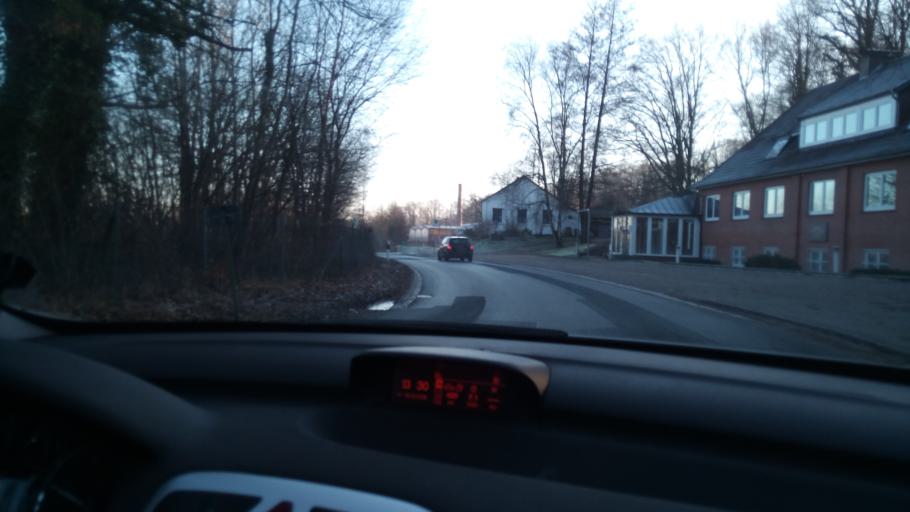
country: DE
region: Schleswig-Holstein
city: Buchhorst
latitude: 53.3820
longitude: 10.5707
